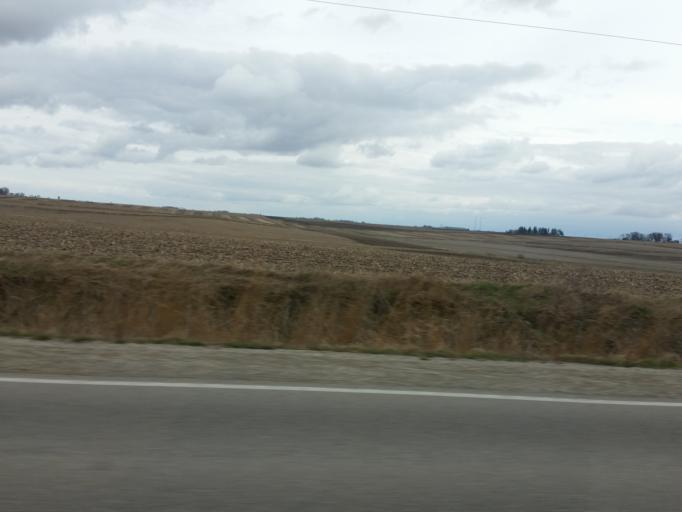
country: US
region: Iowa
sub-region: Black Hawk County
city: Elk Run Heights
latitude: 42.5066
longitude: -92.2196
